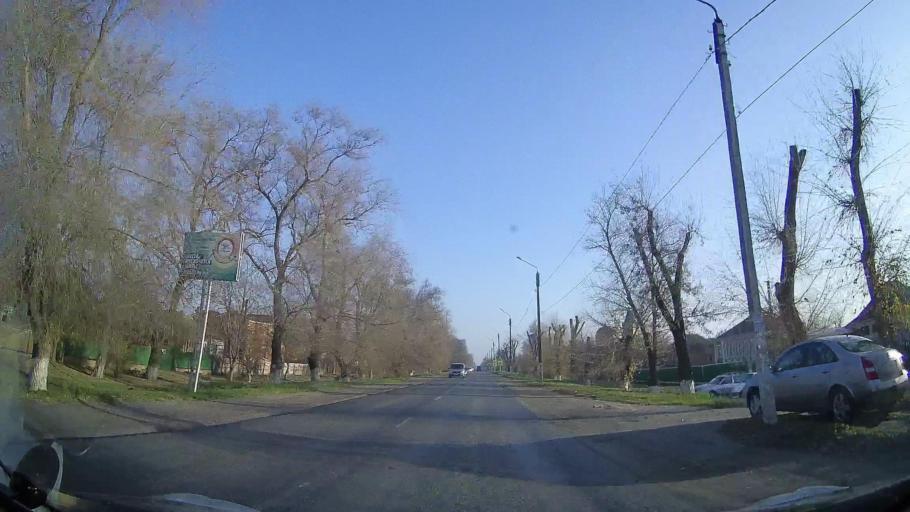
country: RU
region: Rostov
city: Ol'ginskaya
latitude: 47.1951
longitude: 39.9411
